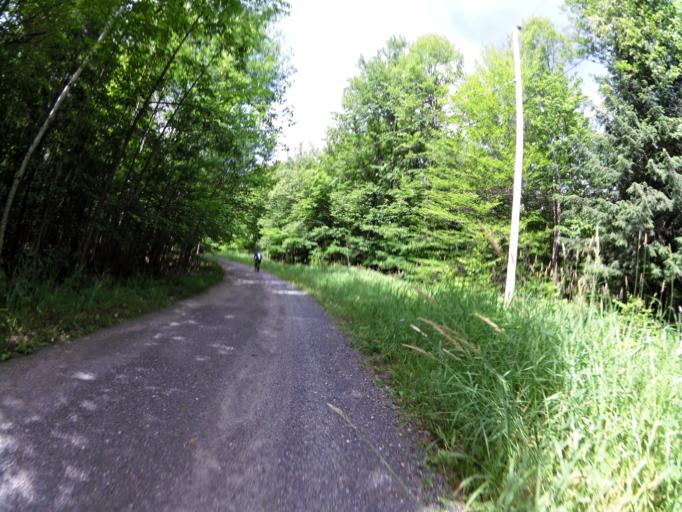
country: CA
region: Ontario
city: Perth
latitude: 45.0610
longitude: -76.4824
